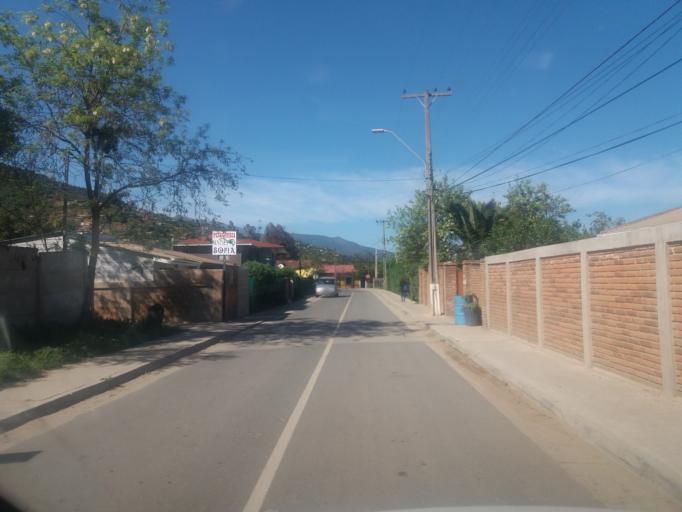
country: CL
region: Valparaiso
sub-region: Provincia de Marga Marga
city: Limache
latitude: -32.9908
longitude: -71.1639
